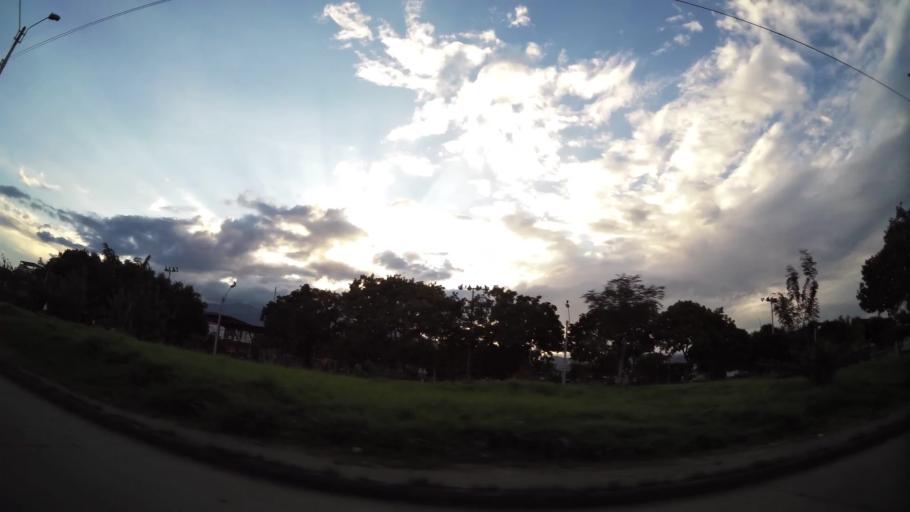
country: CO
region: Valle del Cauca
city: Cali
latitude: 3.4304
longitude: -76.5197
